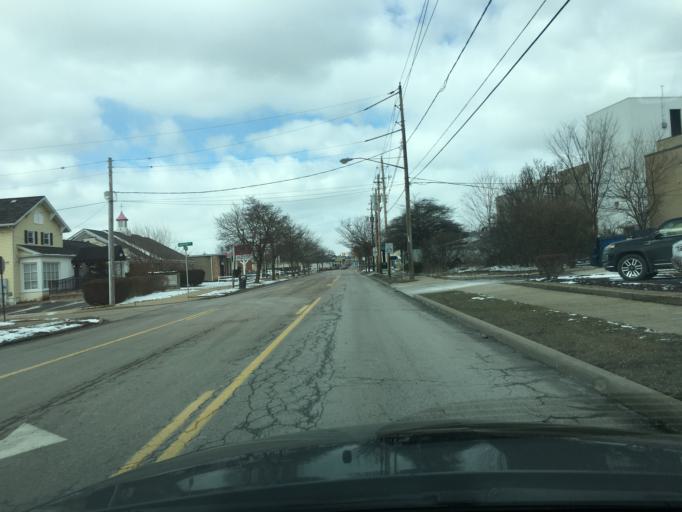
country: US
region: Ohio
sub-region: Summit County
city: Fairlawn
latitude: 41.1075
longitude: -81.5670
